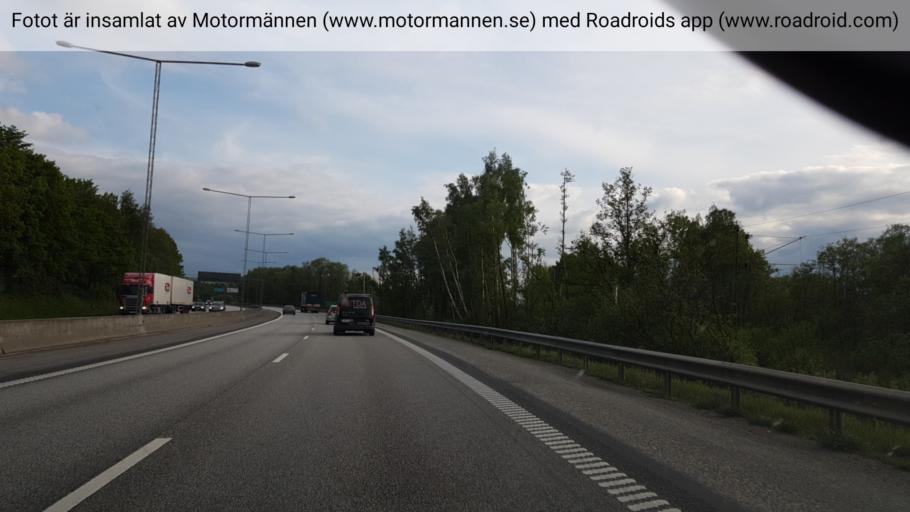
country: SE
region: Joenkoeping
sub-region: Jonkopings Kommun
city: Jonkoping
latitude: 57.7701
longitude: 14.1900
